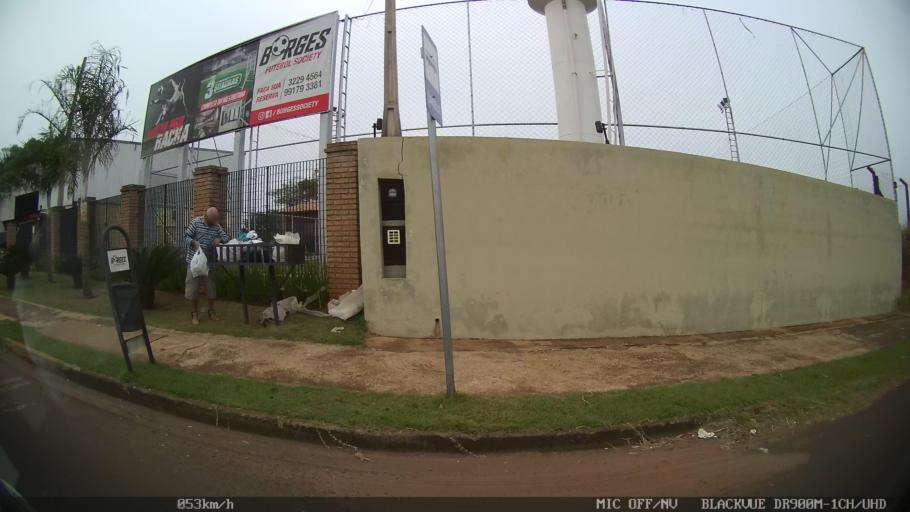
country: BR
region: Sao Paulo
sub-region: Sao Jose Do Rio Preto
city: Sao Jose do Rio Preto
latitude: -20.8567
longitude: -49.3725
